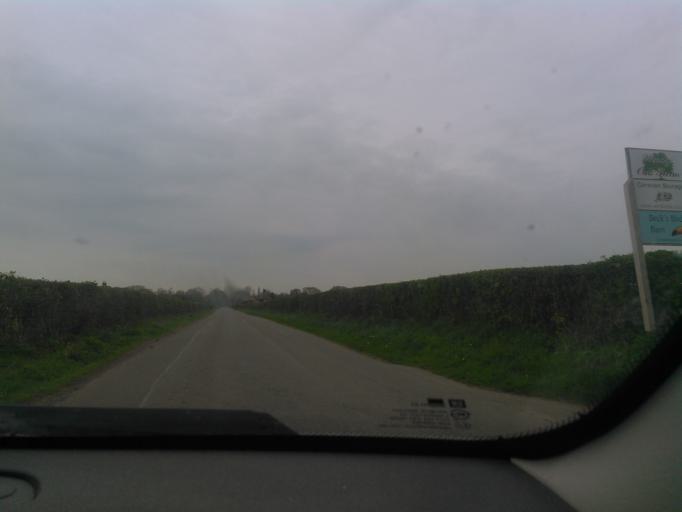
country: GB
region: England
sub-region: Shropshire
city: Stoke upon Tern
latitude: 52.7975
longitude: -2.5800
